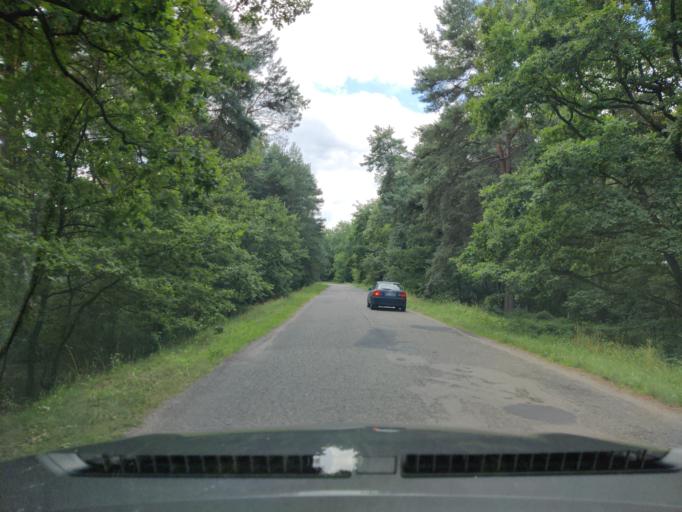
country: PL
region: Masovian Voivodeship
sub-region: Powiat pultuski
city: Pultusk
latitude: 52.7112
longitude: 21.1146
